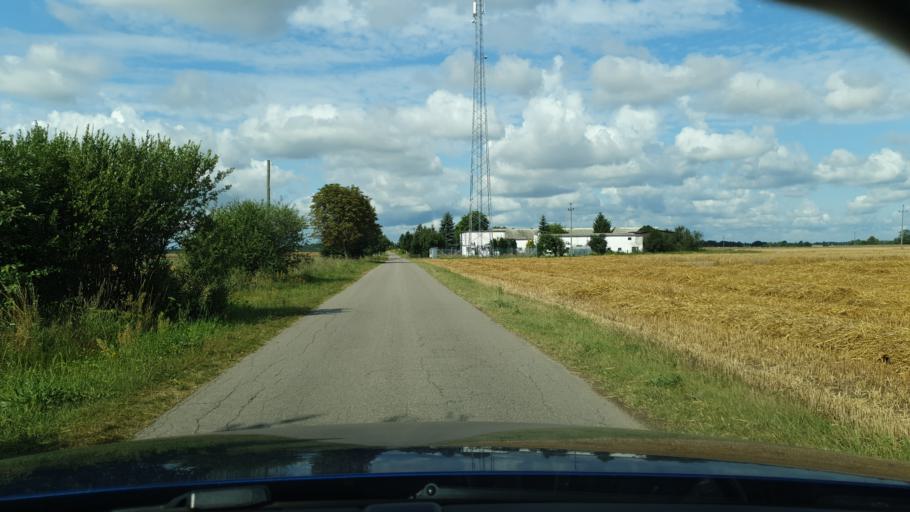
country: PL
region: Pomeranian Voivodeship
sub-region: Powiat czluchowski
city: Przechlewo
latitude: 53.8104
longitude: 17.3969
